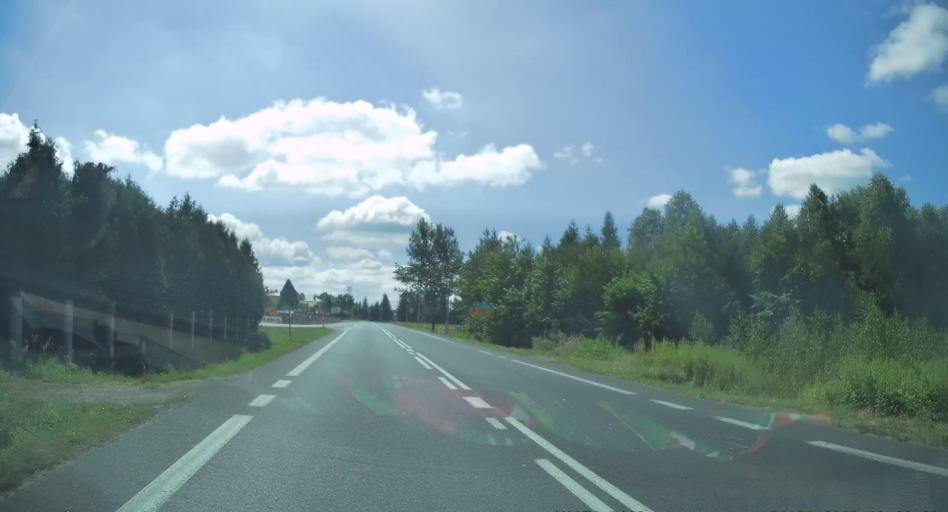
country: PL
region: Subcarpathian Voivodeship
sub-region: Powiat debicki
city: Brzeznica
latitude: 50.1338
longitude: 21.4854
